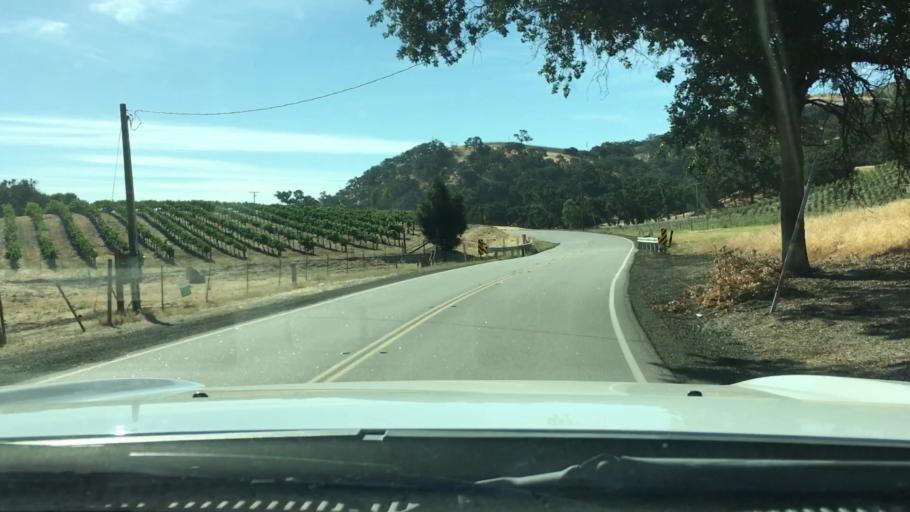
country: US
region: California
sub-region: San Luis Obispo County
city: Templeton
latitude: 35.5630
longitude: -120.6523
